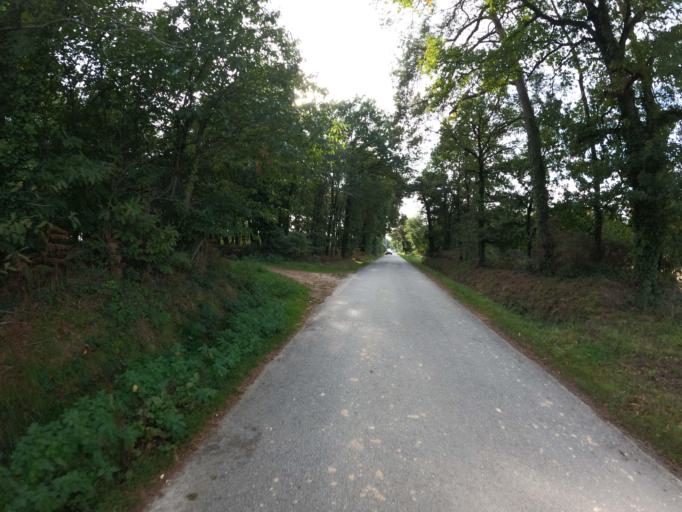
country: FR
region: Brittany
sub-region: Departement du Morbihan
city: Caro
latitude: 47.8827
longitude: -2.3501
